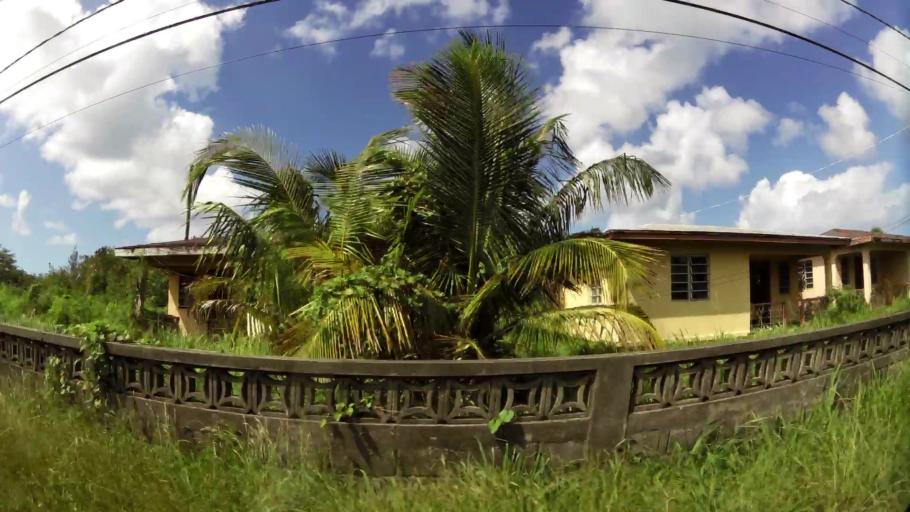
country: KN
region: Saint Thomas Lowland
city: Cotton Ground
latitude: 17.1826
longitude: -62.6201
